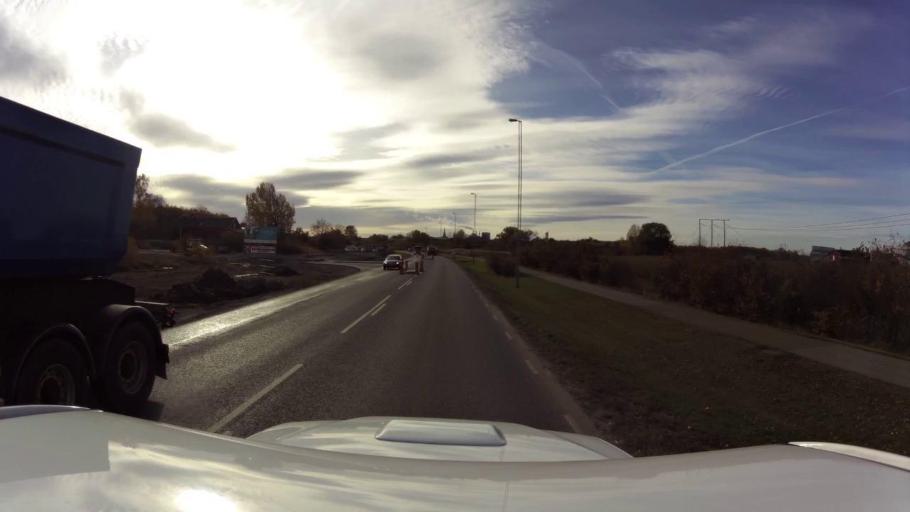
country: SE
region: OEstergoetland
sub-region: Linkopings Kommun
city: Linkoping
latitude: 58.4302
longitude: 15.6409
